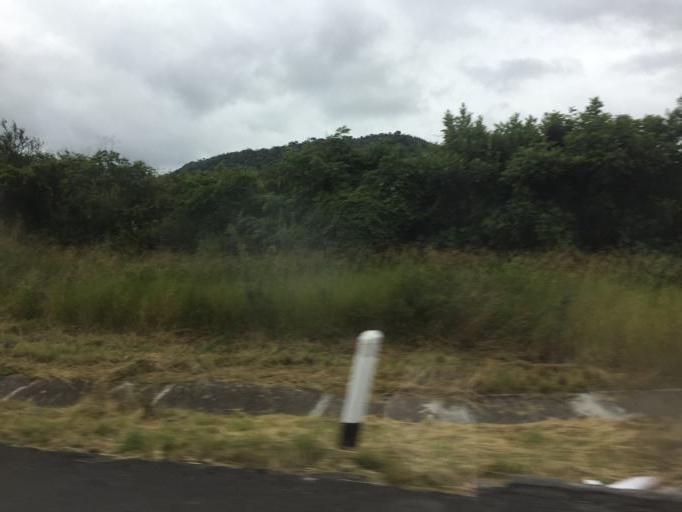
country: MX
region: Jalisco
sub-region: Zapotlan del Rey
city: Zapotlan del Rey
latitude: 20.5168
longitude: -102.9780
